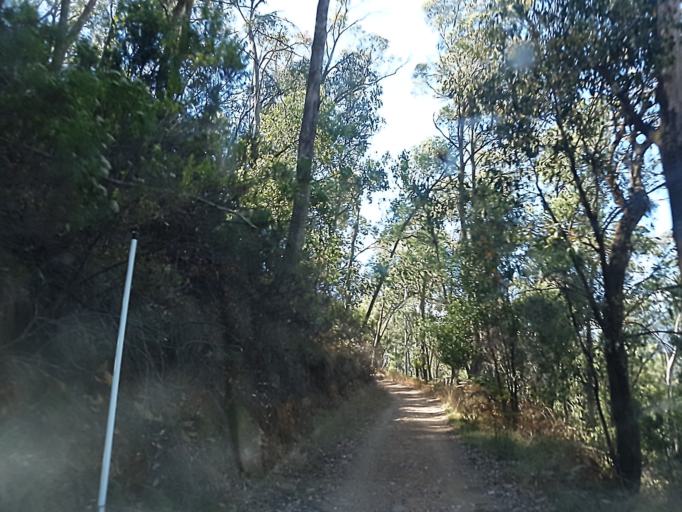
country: AU
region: Victoria
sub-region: Alpine
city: Mount Beauty
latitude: -36.8804
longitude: 147.0414
